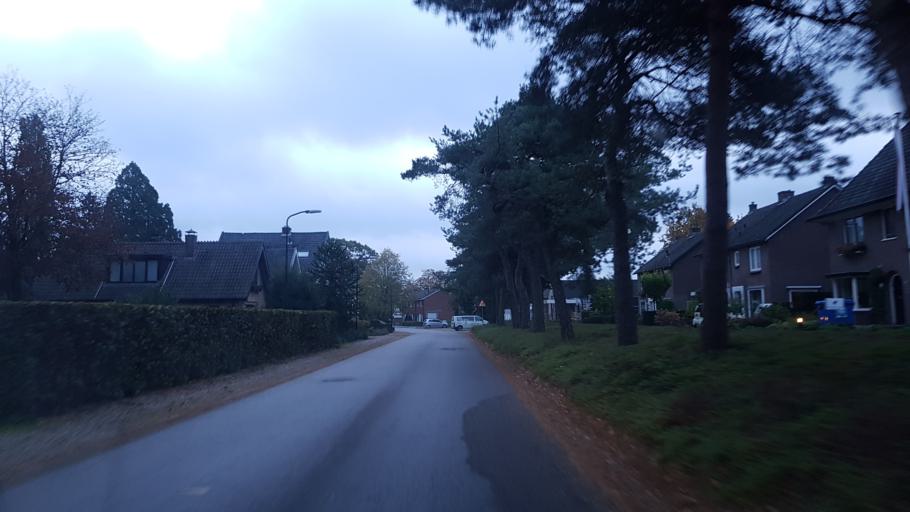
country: NL
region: Gelderland
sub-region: Gemeente Apeldoorn
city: Apeldoorn
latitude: 52.2146
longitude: 5.9421
